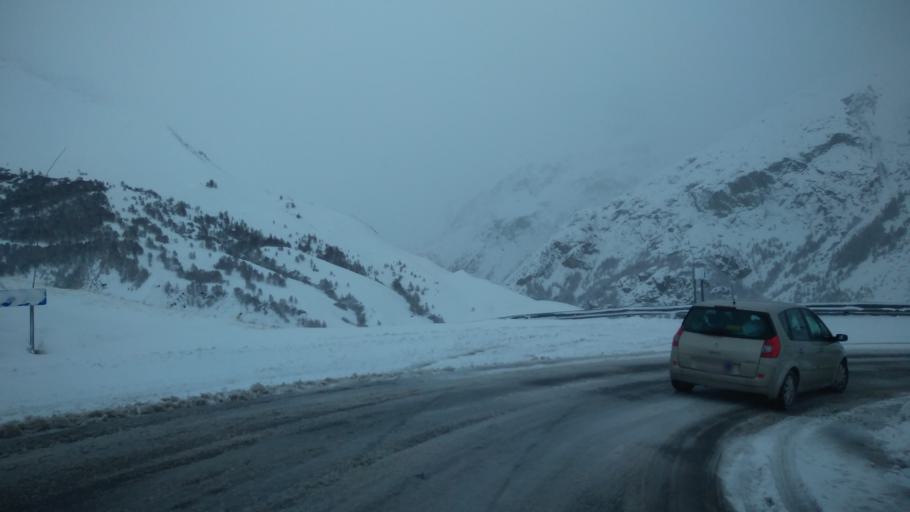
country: FR
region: Rhone-Alpes
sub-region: Departement de la Savoie
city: Valloire
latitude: 45.0361
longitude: 6.3682
